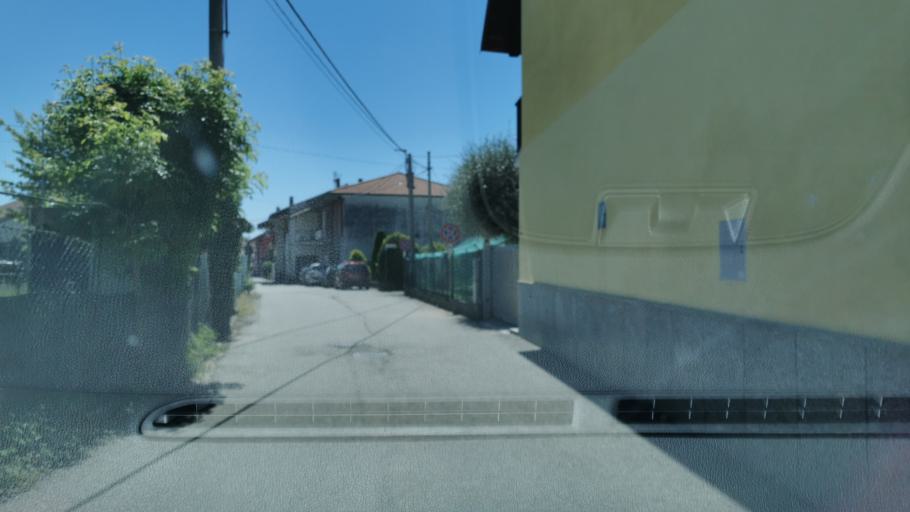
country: IT
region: Piedmont
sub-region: Provincia di Torino
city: Barbania
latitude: 45.2843
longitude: 7.6425
